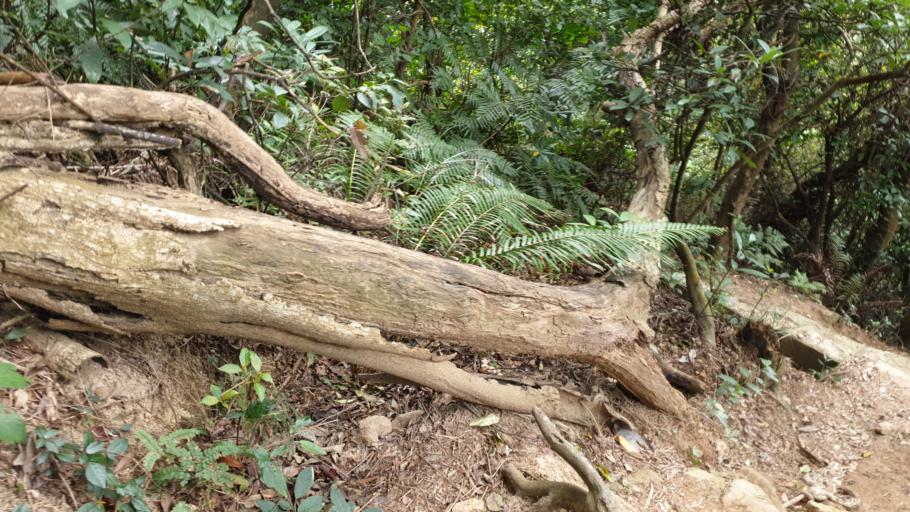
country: TW
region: Taipei
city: Taipei
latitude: 25.0919
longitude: 121.5462
